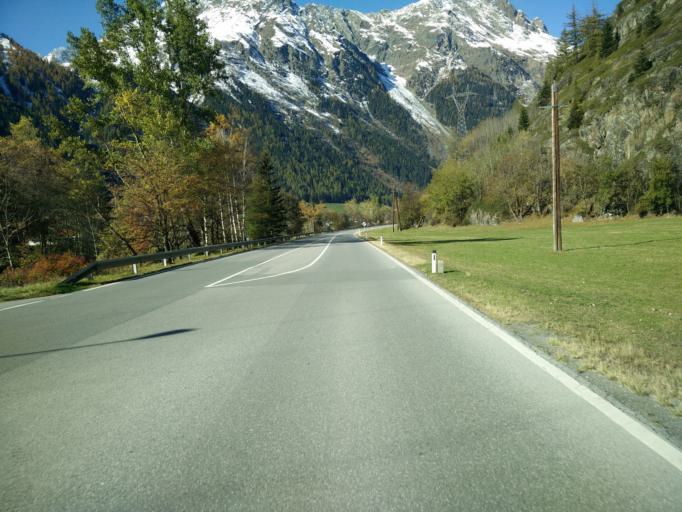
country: AT
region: Tyrol
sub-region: Politischer Bezirk Imst
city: Soelden
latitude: 47.0407
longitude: 10.9788
